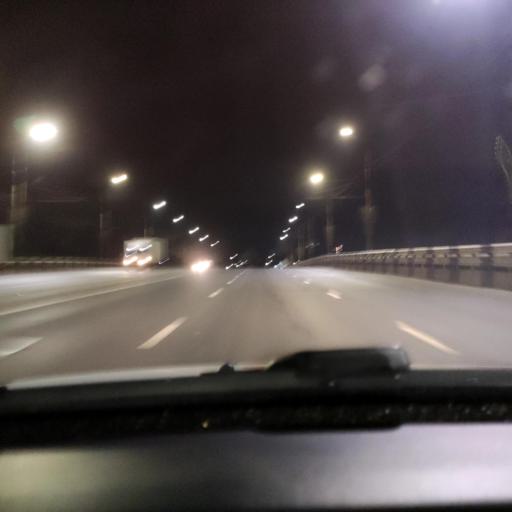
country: RU
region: Voronezj
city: Voronezh
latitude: 51.6340
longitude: 39.2215
